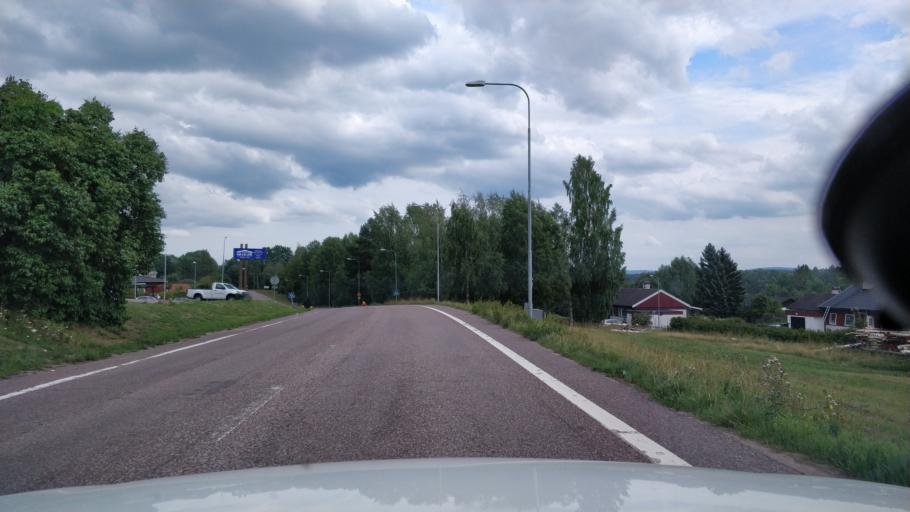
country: SE
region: Dalarna
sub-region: Faluns Kommun
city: Bjursas
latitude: 60.7372
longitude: 15.4511
